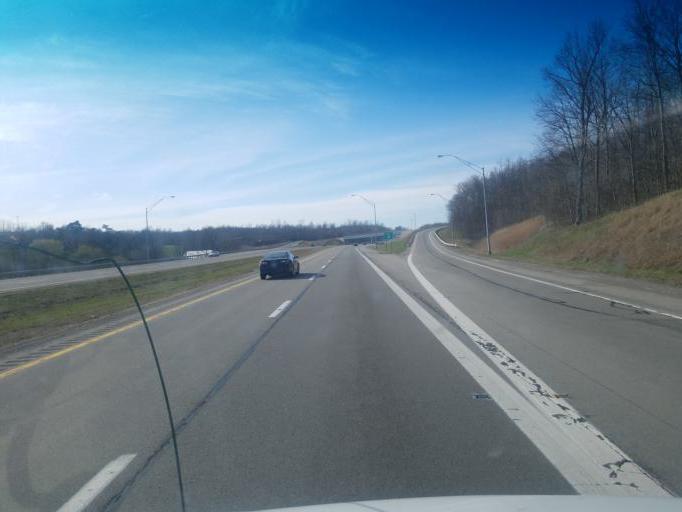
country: US
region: Ohio
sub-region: Logan County
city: Bellefontaine
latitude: 40.3390
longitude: -83.6907
